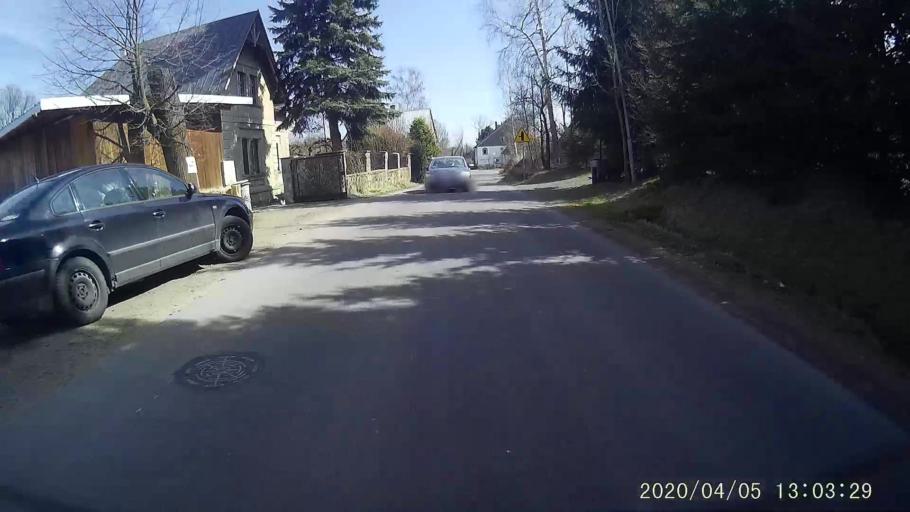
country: PL
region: Lower Silesian Voivodeship
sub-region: Powiat lwowecki
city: Mirsk
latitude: 50.9775
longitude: 15.3530
